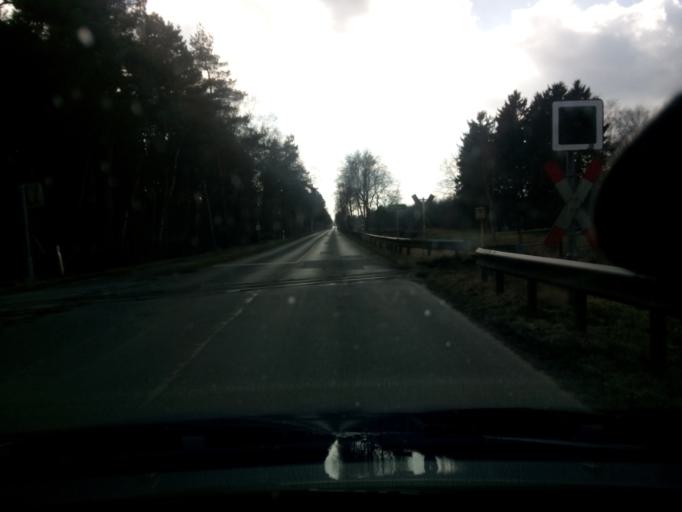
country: DE
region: Lower Saxony
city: Gnarrenburg
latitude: 53.3821
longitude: 9.0196
